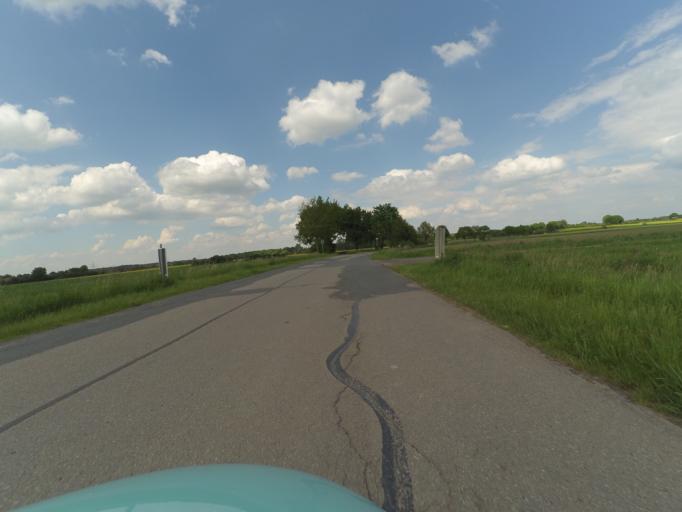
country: DE
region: Lower Saxony
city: Lehrte
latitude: 52.3659
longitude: 10.0235
